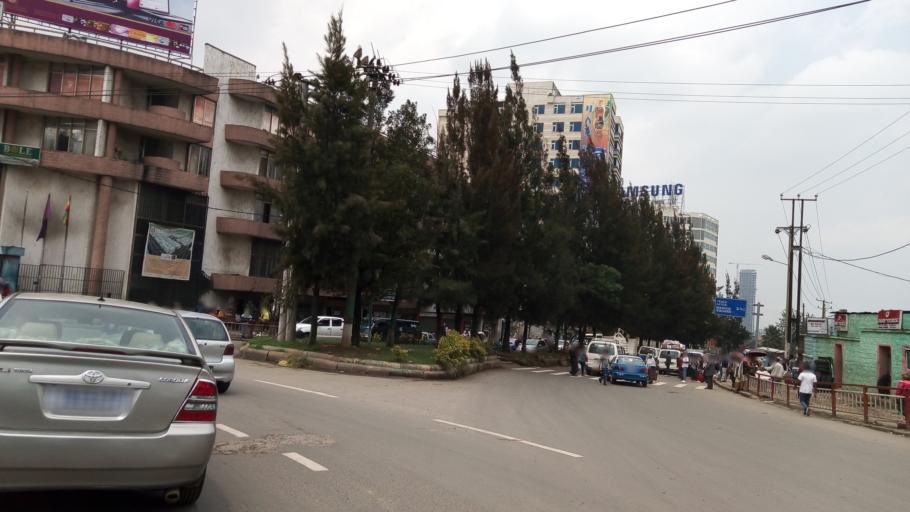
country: ET
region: Adis Abeba
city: Addis Ababa
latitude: 9.0283
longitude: 38.7434
